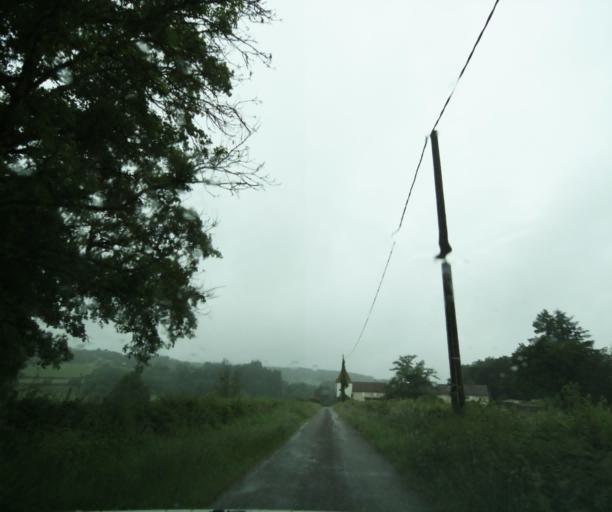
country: FR
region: Bourgogne
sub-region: Departement de Saone-et-Loire
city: Charolles
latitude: 46.3902
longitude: 4.3288
